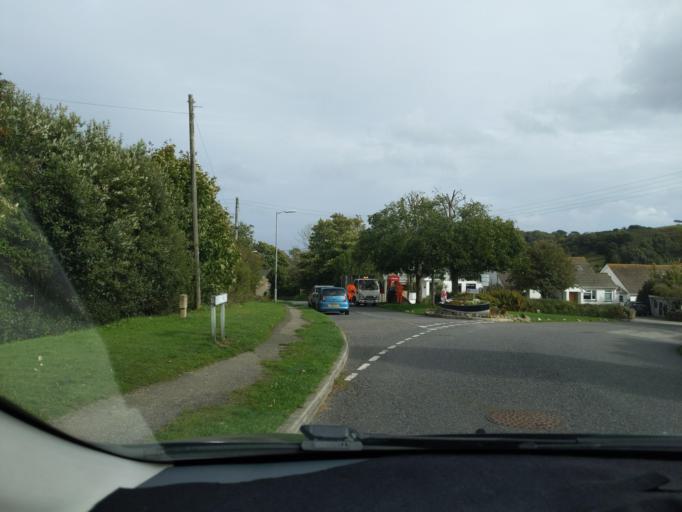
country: GB
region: England
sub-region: Cornwall
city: Mevagissey
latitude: 50.2405
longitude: -4.7964
